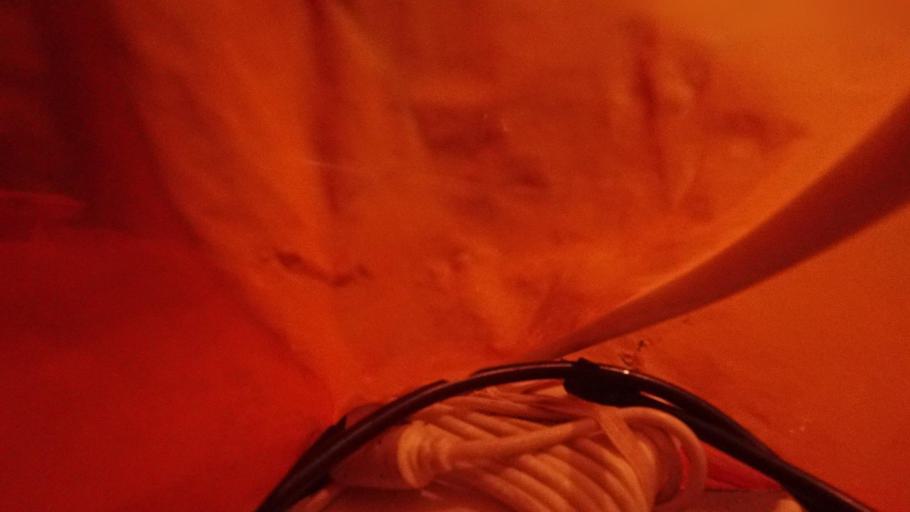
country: RU
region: Jewish Autonomous Oblast
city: Khingansk
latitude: 49.1636
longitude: 130.7652
